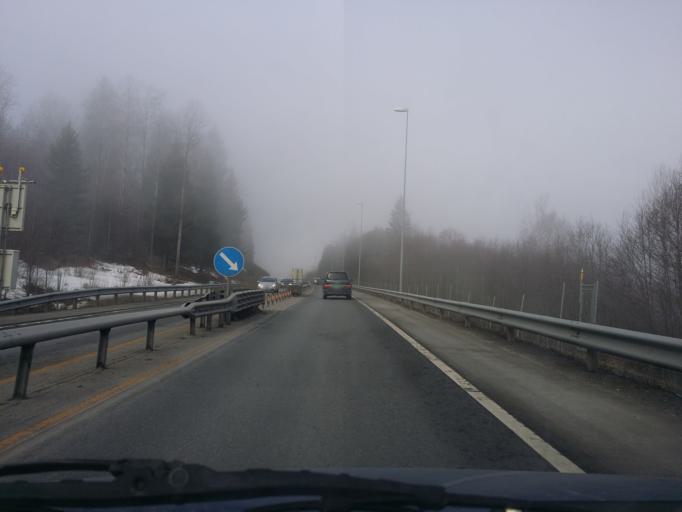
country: NO
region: Buskerud
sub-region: Drammen
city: Drammen
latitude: 59.7416
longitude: 10.1345
